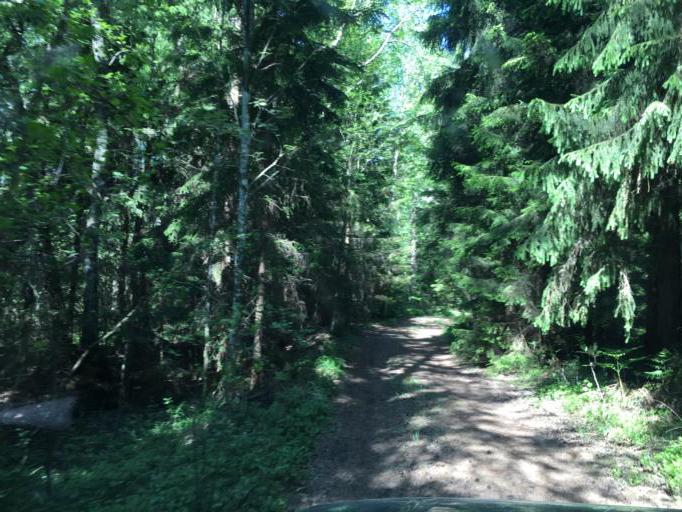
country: LV
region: Ventspils
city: Ventspils
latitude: 57.4704
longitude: 21.7717
